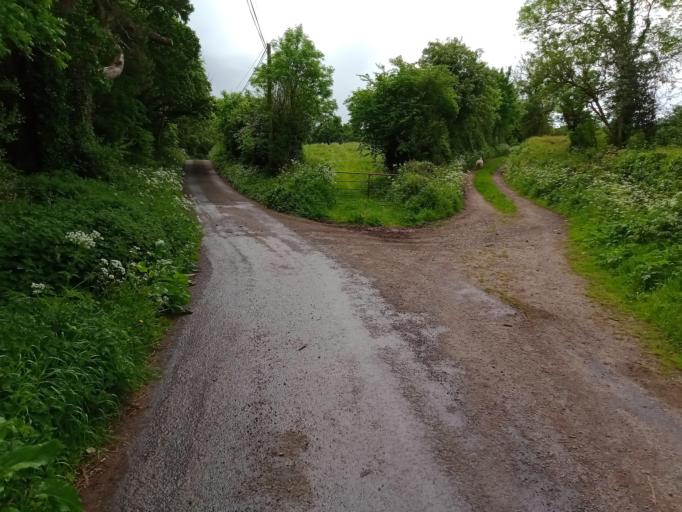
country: IE
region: Leinster
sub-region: Kilkenny
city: Thomastown
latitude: 52.5100
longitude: -7.1313
